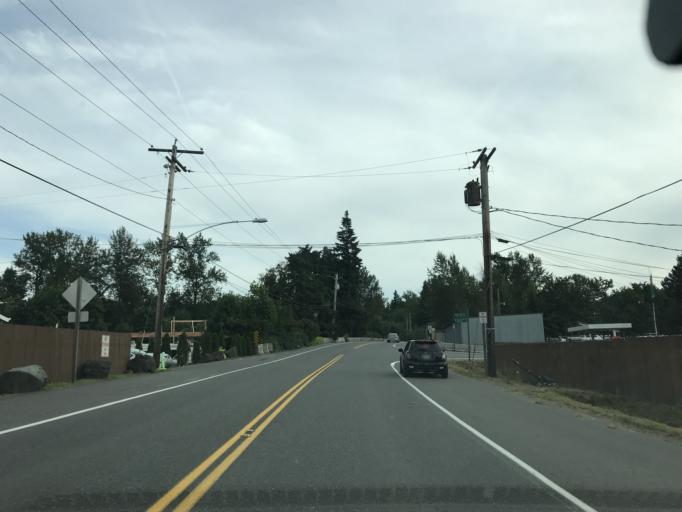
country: US
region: Washington
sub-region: King County
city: Fall City
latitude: 47.5659
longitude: -121.8882
